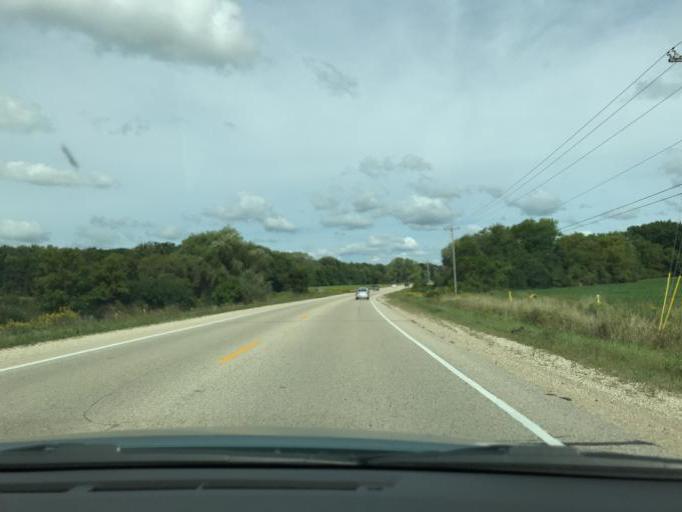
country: US
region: Wisconsin
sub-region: Racine County
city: Bohners Lake
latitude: 42.6284
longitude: -88.2455
